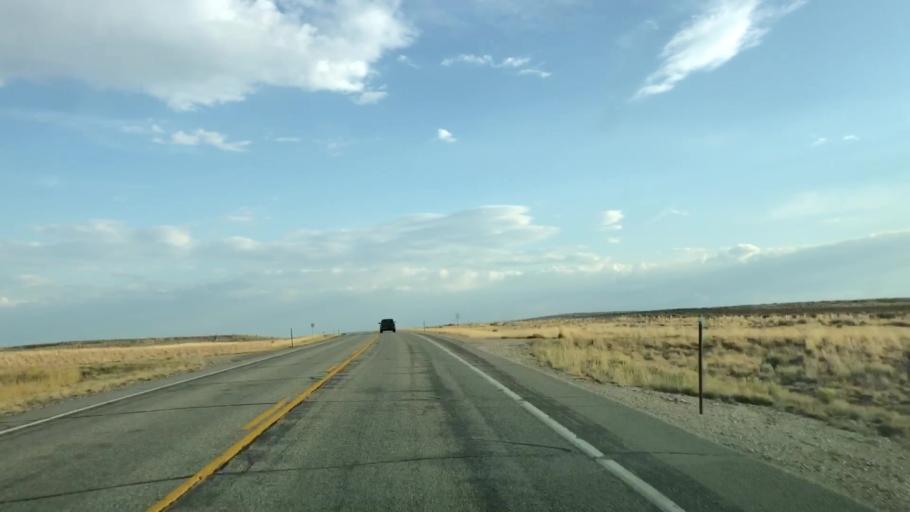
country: US
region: Wyoming
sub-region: Sublette County
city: Pinedale
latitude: 42.3431
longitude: -109.5219
